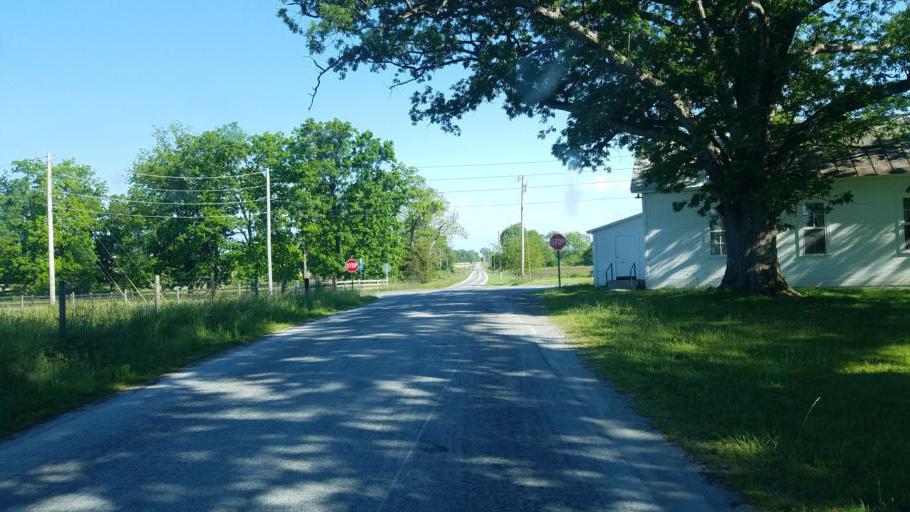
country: US
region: Ohio
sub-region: Hardin County
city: Kenton
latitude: 40.5872
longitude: -83.4737
